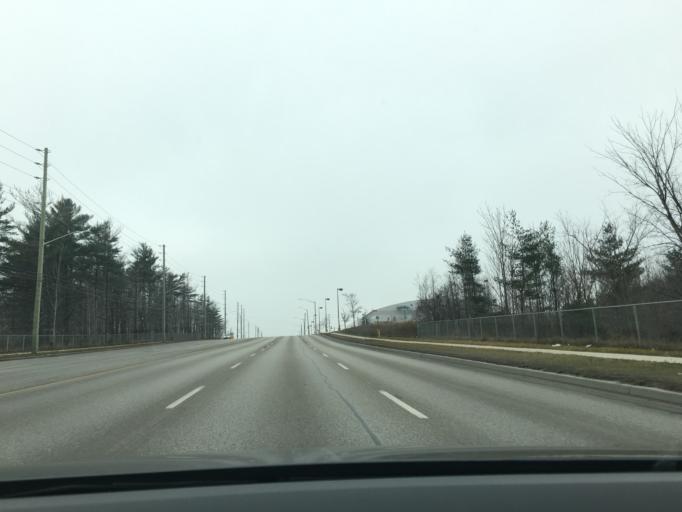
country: CA
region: Ontario
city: Innisfil
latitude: 44.3380
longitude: -79.6739
